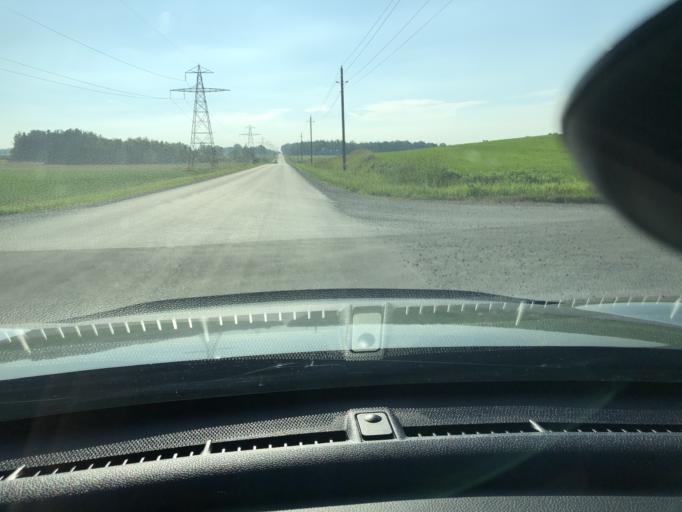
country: CA
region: Ontario
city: Stratford
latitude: 43.3882
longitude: -80.8626
